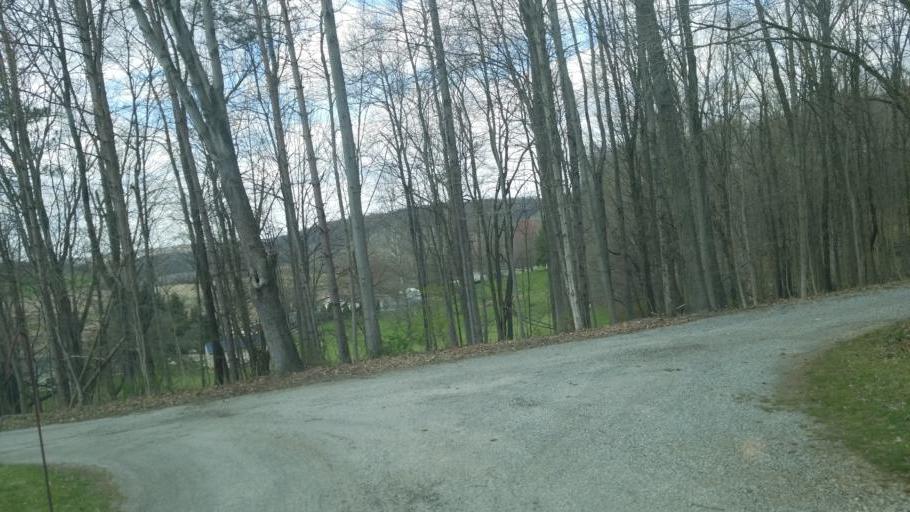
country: US
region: Ohio
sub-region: Knox County
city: Mount Vernon
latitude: 40.4407
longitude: -82.4431
